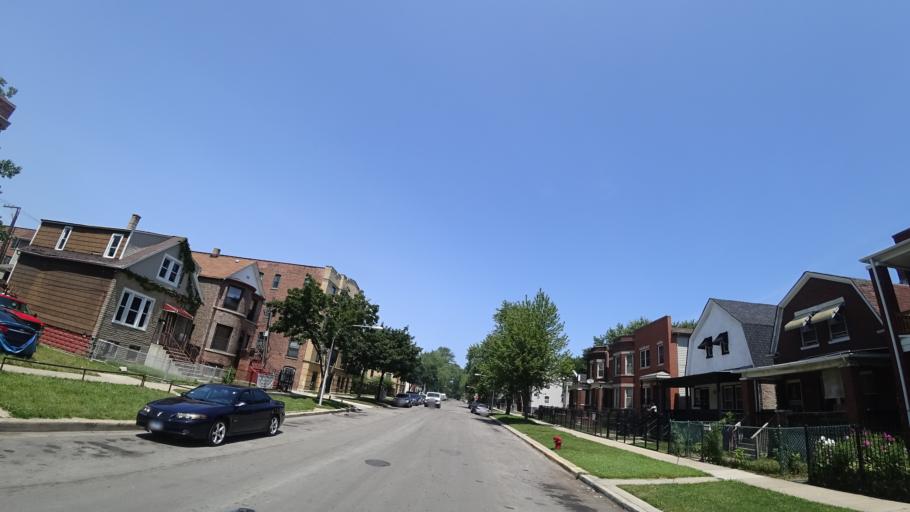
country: US
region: Illinois
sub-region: Cook County
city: Chicago
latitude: 41.7704
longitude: -87.5911
